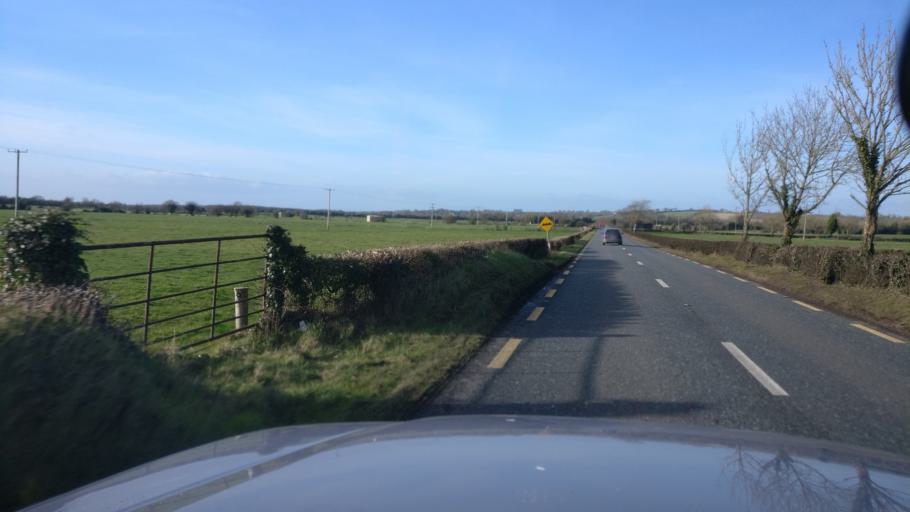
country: IE
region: Leinster
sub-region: Laois
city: Mountmellick
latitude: 53.1778
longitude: -7.3906
